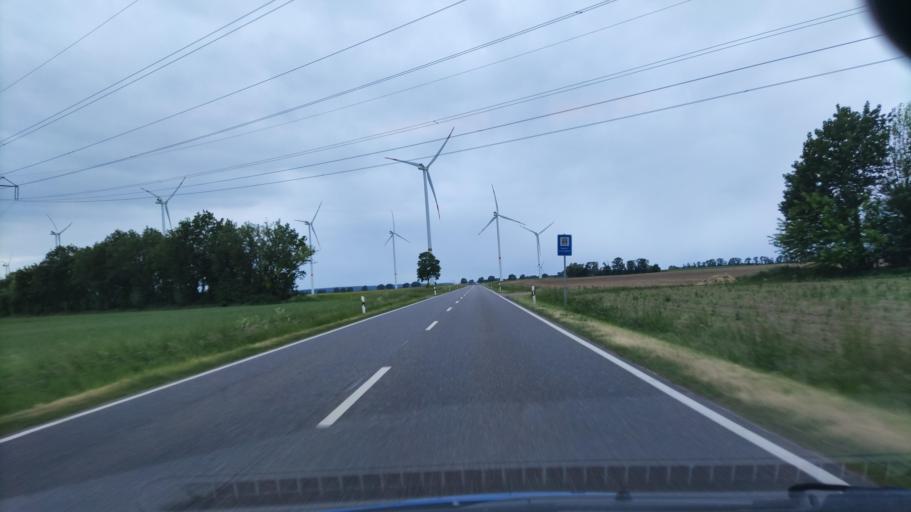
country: DE
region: Mecklenburg-Vorpommern
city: Neuburg
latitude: 53.4454
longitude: 11.9188
